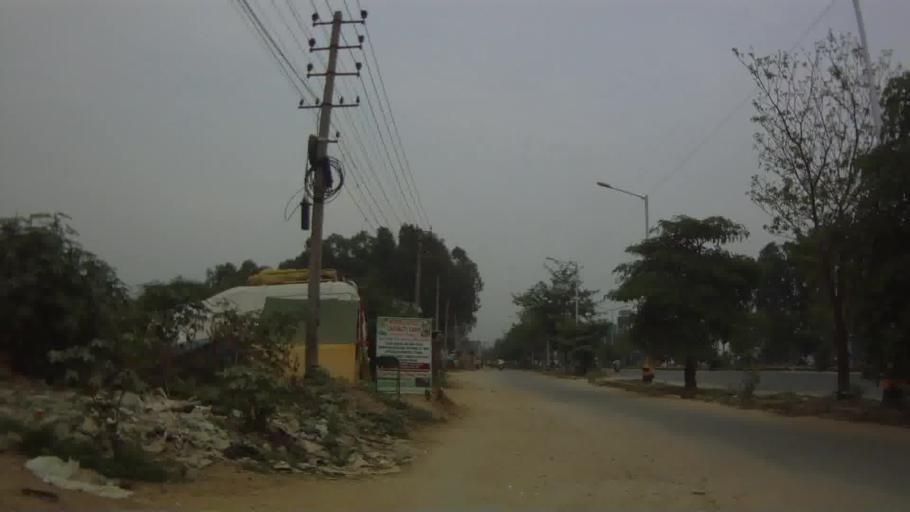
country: IN
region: Karnataka
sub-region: Bangalore Urban
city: Bangalore
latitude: 12.9775
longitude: 77.6963
